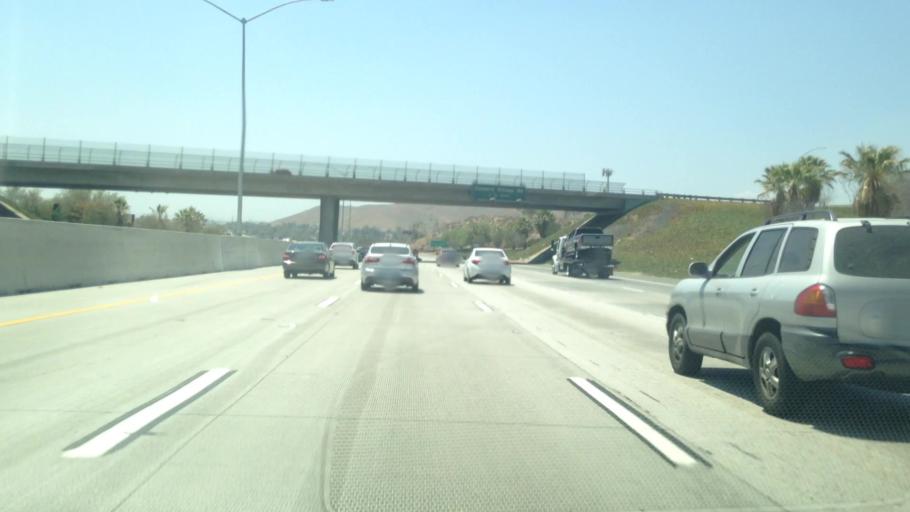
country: US
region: California
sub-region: Riverside County
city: Glen Avon
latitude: 34.0191
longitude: -117.4791
